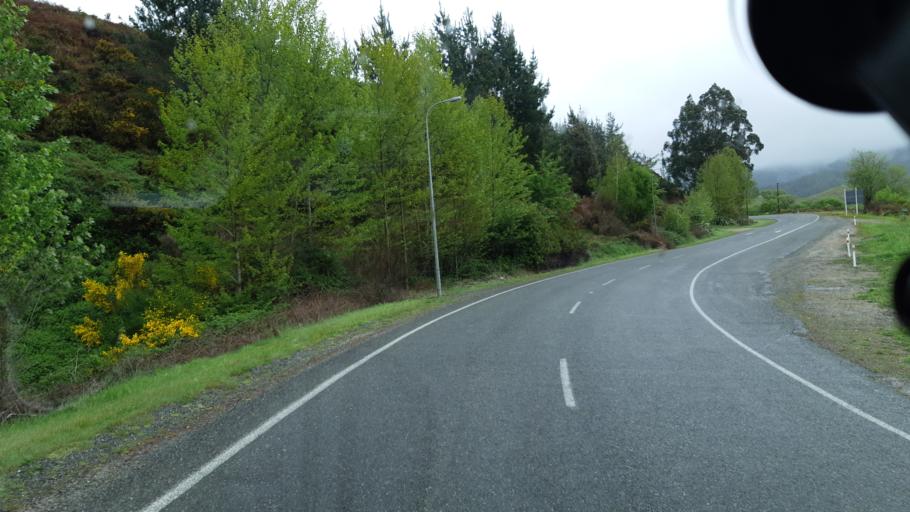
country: NZ
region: West Coast
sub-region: Buller District
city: Westport
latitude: -42.1216
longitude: 171.8613
